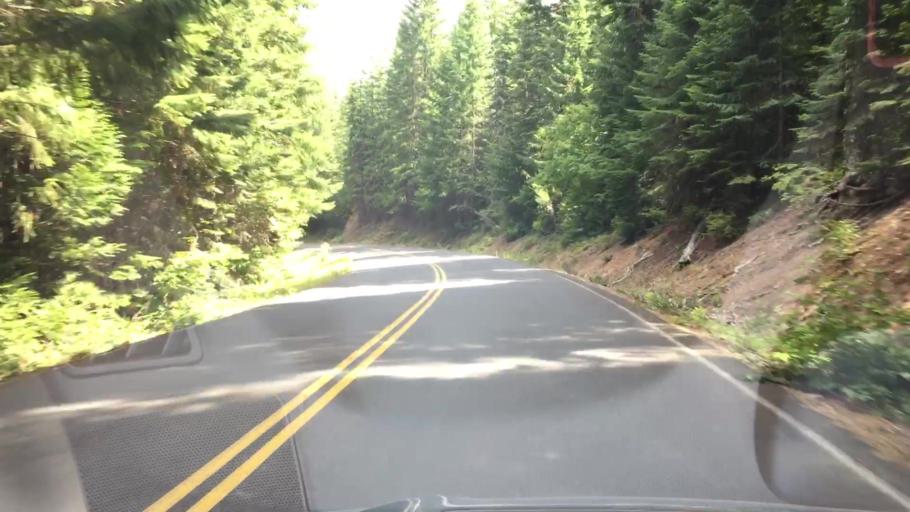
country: US
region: Washington
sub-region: Klickitat County
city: White Salmon
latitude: 46.0825
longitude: -121.5971
